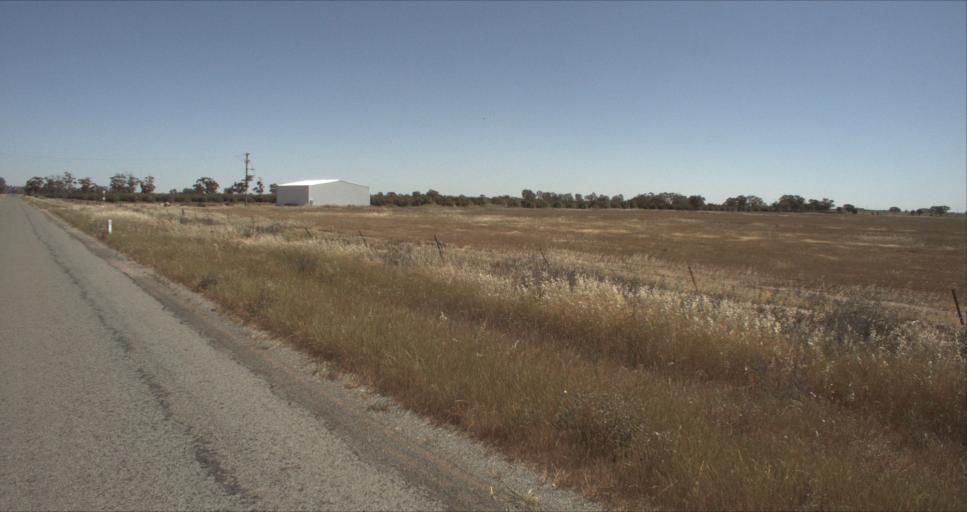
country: AU
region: New South Wales
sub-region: Leeton
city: Leeton
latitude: -34.4863
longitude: 146.4142
